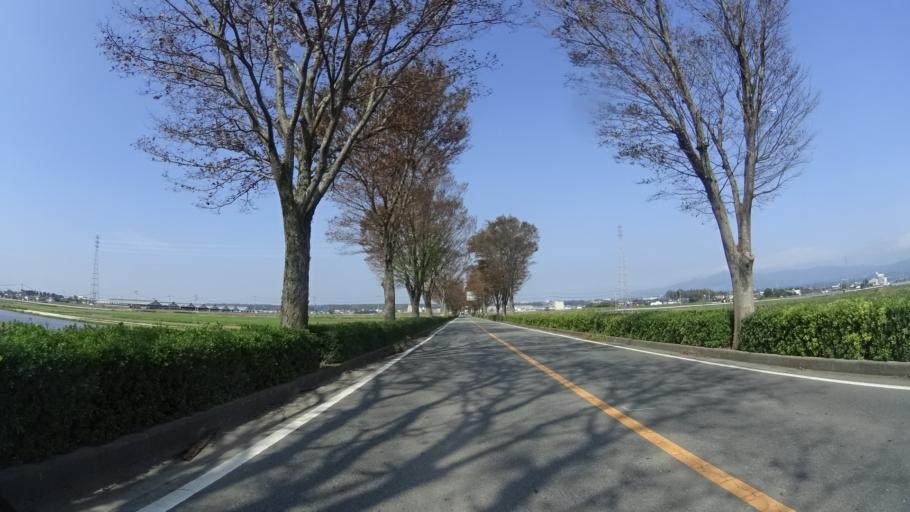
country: JP
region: Kumamoto
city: Ozu
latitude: 32.8592
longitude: 130.8553
